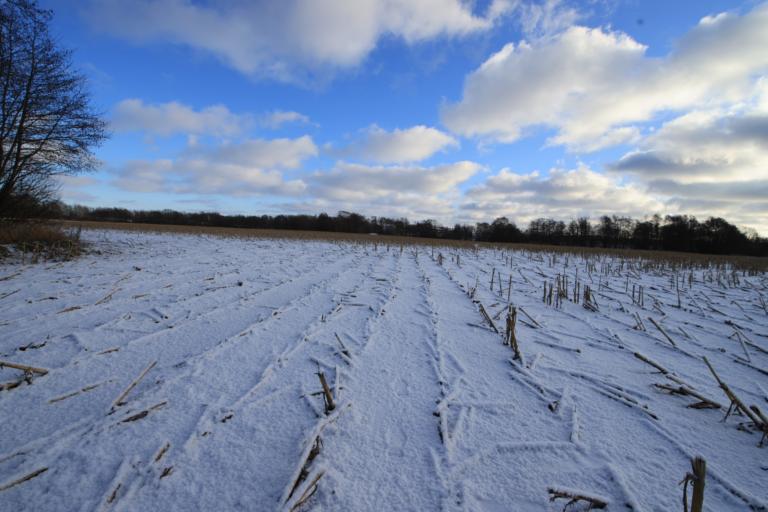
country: SE
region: Halland
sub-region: Varbergs Kommun
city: Varberg
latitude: 57.1324
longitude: 12.2880
